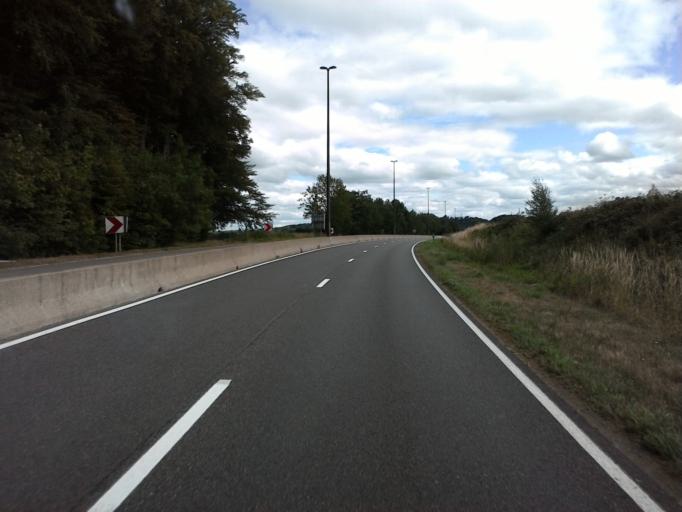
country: BE
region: Wallonia
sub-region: Province du Luxembourg
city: Attert
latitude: 49.7322
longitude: 5.7924
